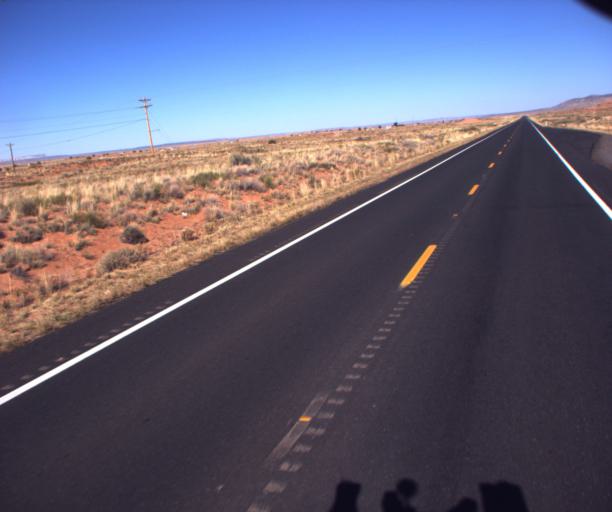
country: US
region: Arizona
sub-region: Coconino County
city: Tuba City
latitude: 36.2993
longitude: -110.9786
